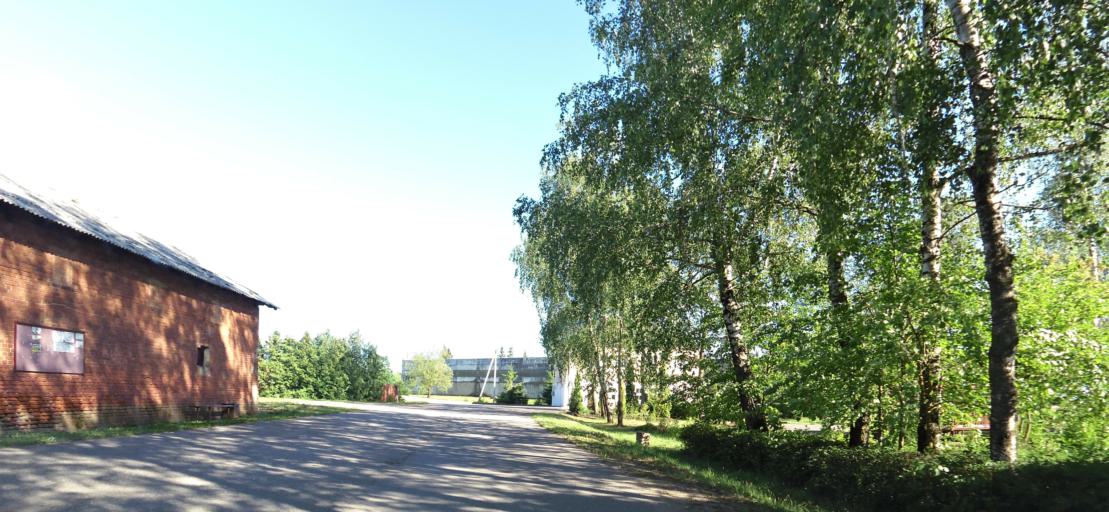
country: LT
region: Panevezys
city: Pasvalys
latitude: 56.1322
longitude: 24.5419
